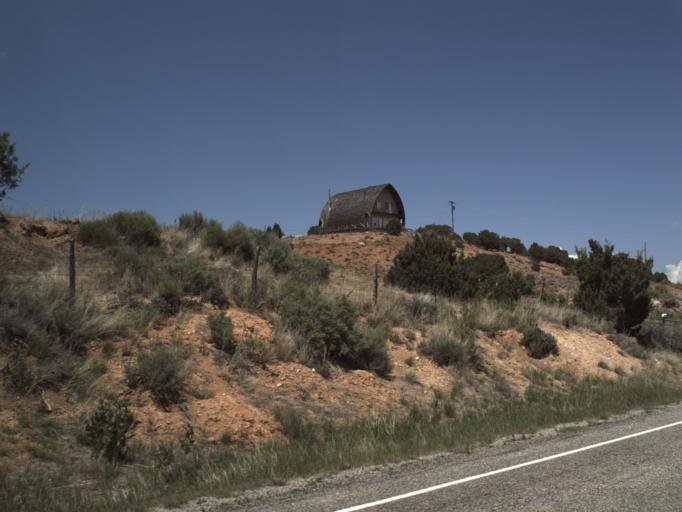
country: US
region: Utah
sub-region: Rich County
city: Randolph
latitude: 41.5125
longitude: -111.2198
